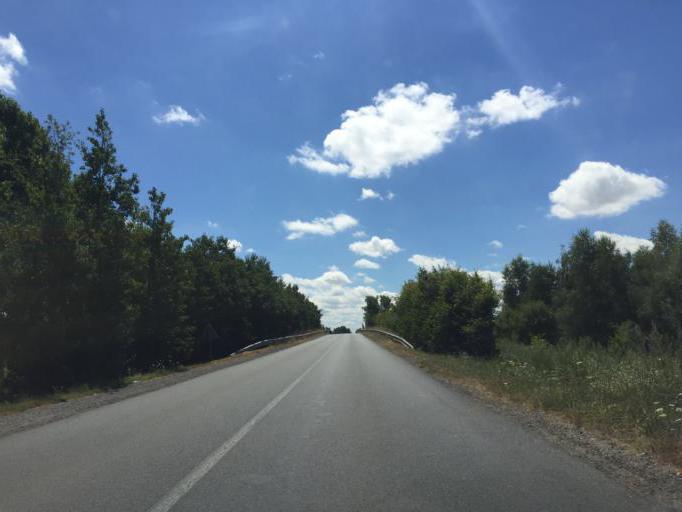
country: FR
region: Auvergne
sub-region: Departement de l'Allier
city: Moulins
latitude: 46.5926
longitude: 3.3317
